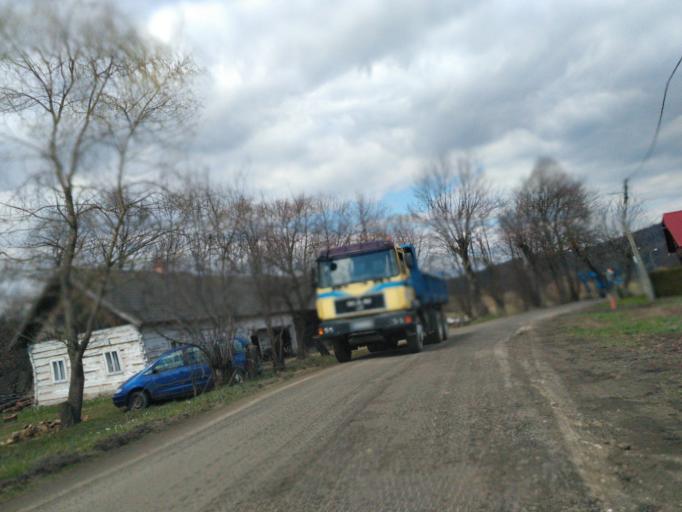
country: PL
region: Subcarpathian Voivodeship
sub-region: Powiat sanocki
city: Tyrawa Woloska
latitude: 49.6479
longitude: 22.2983
